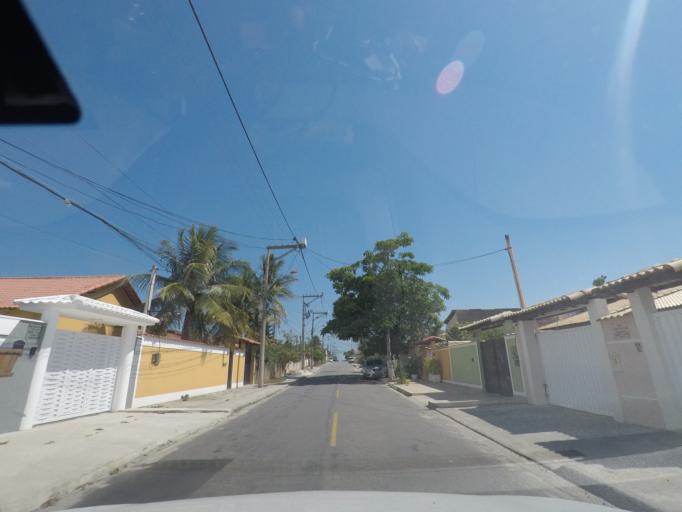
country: BR
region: Rio de Janeiro
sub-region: Marica
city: Marica
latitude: -22.9629
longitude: -42.9649
